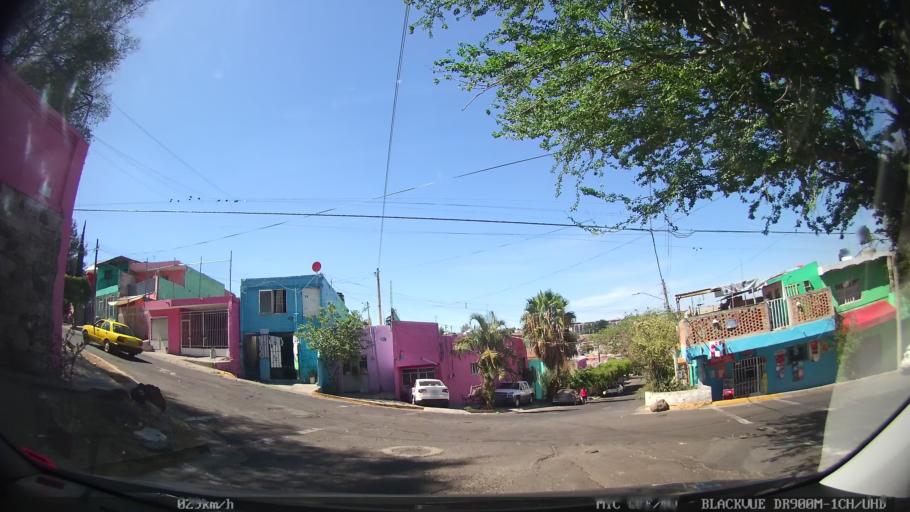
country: MX
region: Jalisco
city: Tlaquepaque
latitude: 20.6916
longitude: -103.2803
